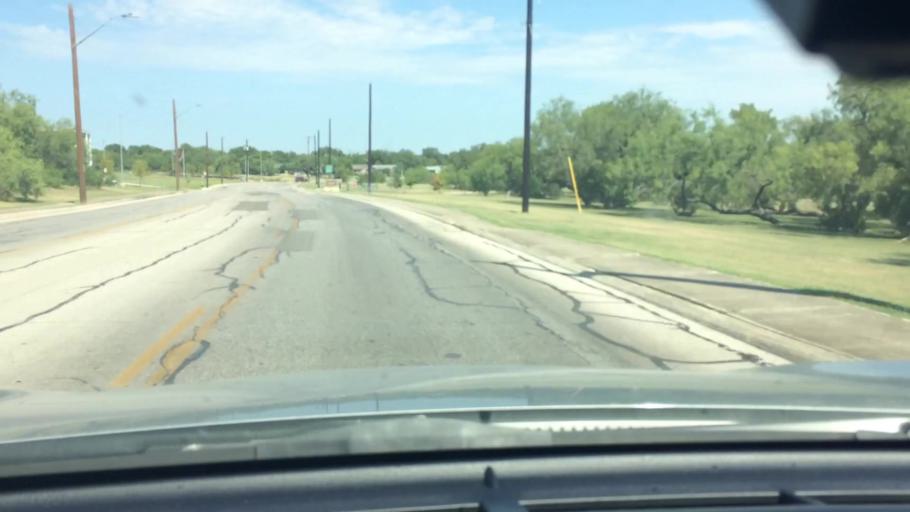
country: US
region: Texas
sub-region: Bexar County
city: San Antonio
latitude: 29.3876
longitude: -98.4312
